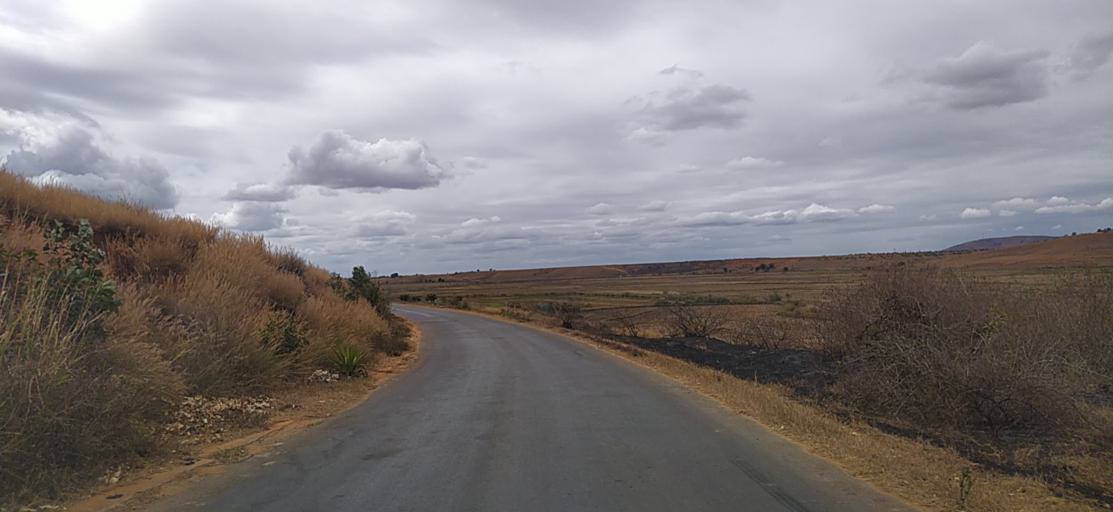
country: MG
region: Alaotra Mangoro
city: Ambatondrazaka
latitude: -17.9255
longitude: 48.2582
